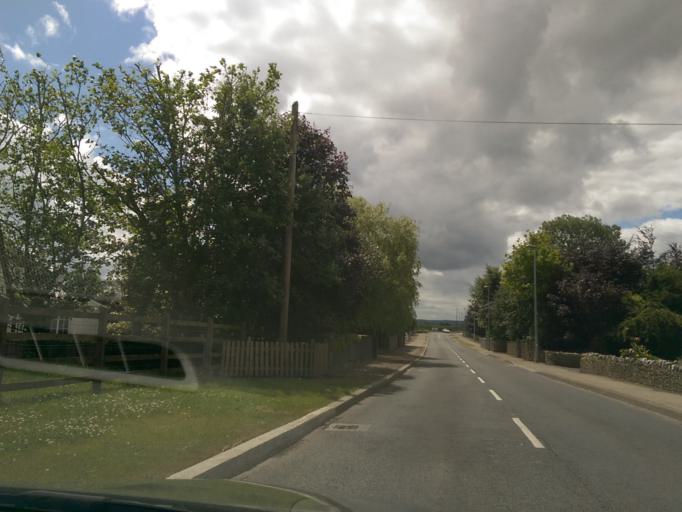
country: IE
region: Munster
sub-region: North Tipperary
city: Nenagh
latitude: 52.8524
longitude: -8.2068
